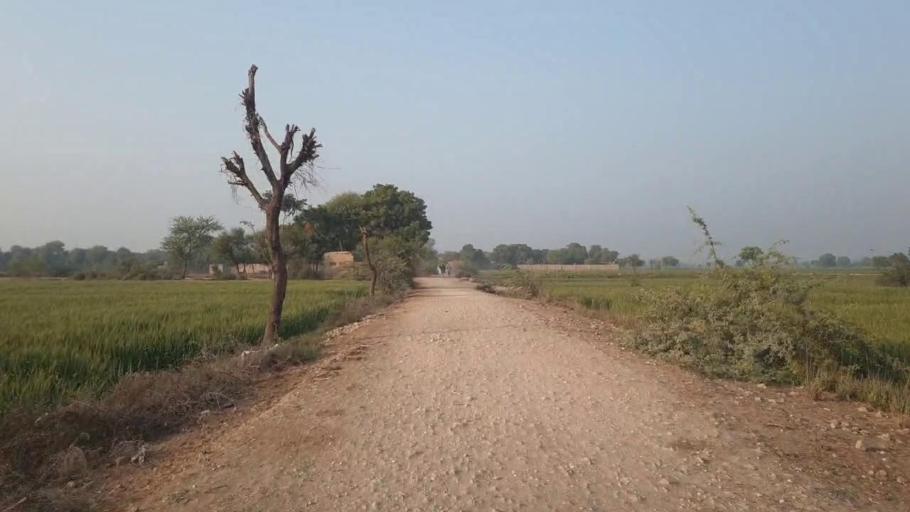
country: PK
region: Sindh
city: Bhit Shah
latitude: 25.8105
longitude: 68.4769
